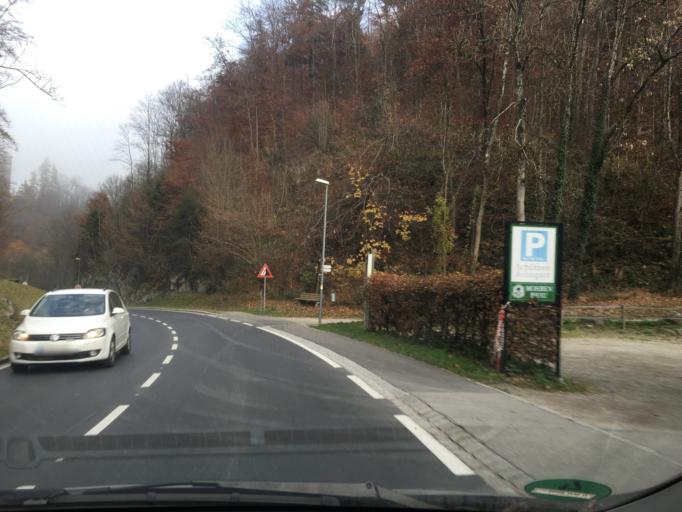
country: AT
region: Vorarlberg
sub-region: Politischer Bezirk Feldkirch
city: Gotzis
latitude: 47.3256
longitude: 9.6441
